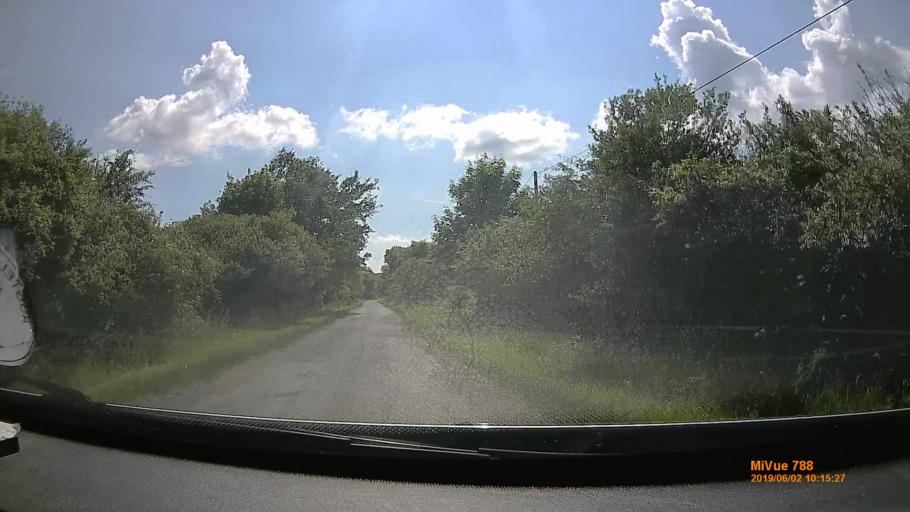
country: HU
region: Borsod-Abauj-Zemplen
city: Szendro
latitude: 48.5071
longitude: 20.8008
